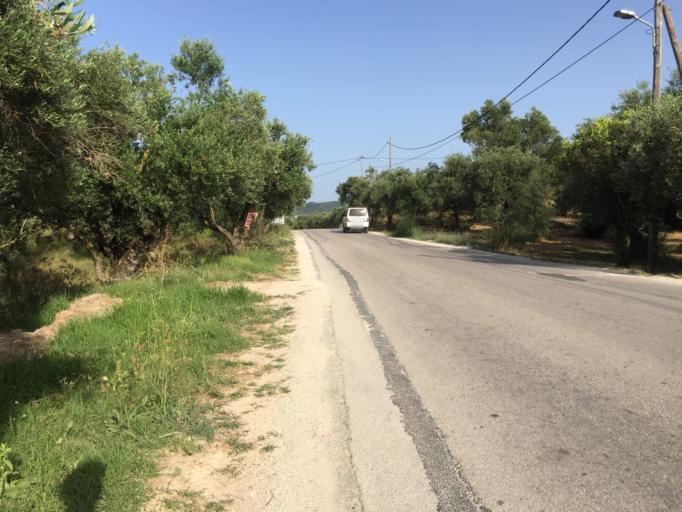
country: GR
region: Ionian Islands
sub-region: Nomos Zakynthou
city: Vanaton
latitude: 37.8215
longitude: 20.8549
